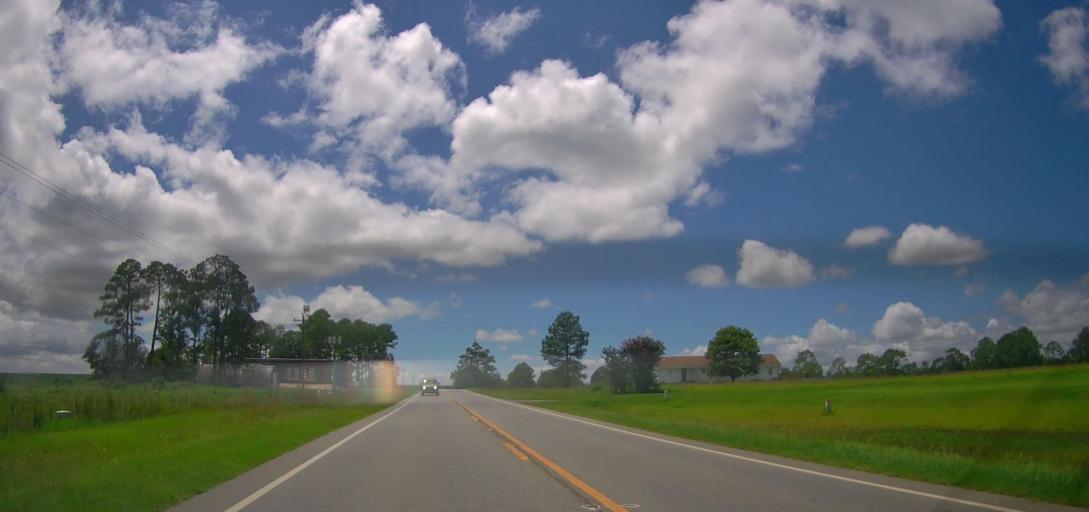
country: US
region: Georgia
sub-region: Turner County
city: Ashburn
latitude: 31.7184
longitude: -83.6011
